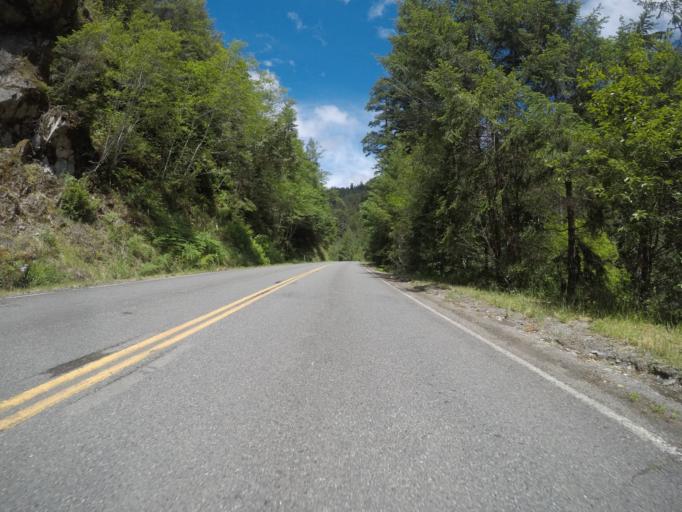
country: US
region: California
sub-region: Del Norte County
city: Bertsch-Oceanview
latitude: 41.7936
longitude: -124.0341
